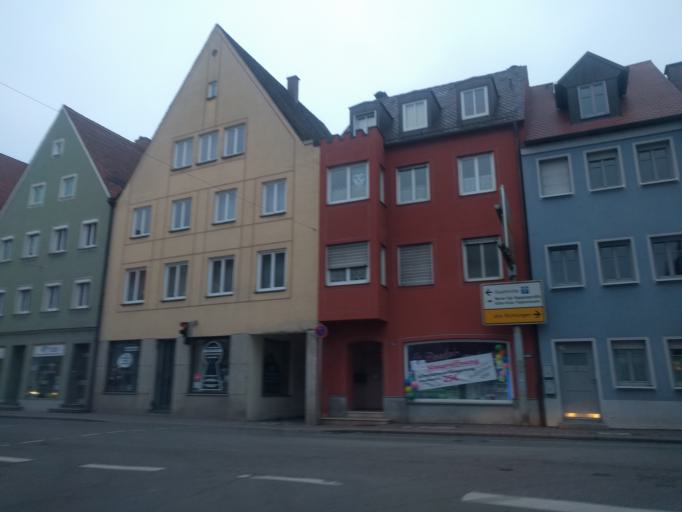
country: DE
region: Bavaria
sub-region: Swabia
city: Donauwoerth
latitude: 48.7169
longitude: 10.7824
